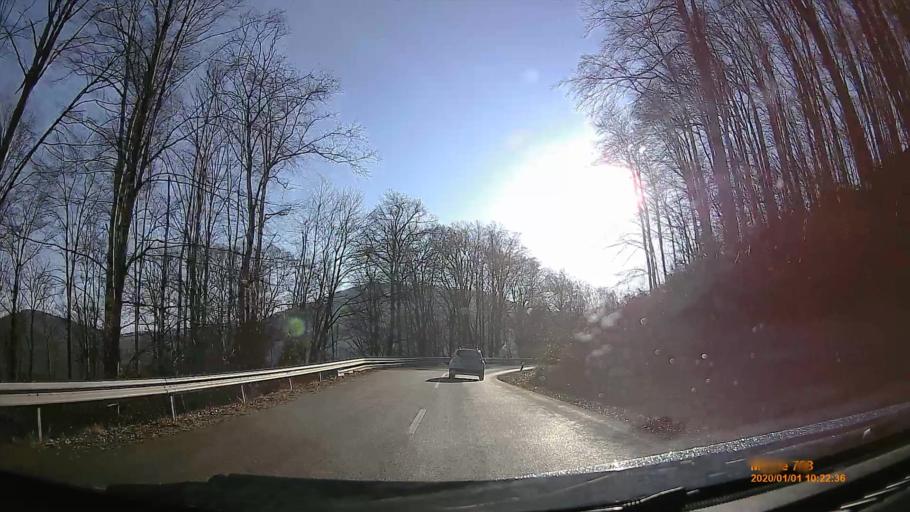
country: HU
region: Heves
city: Paradsasvar
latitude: 47.8961
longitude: 19.9782
